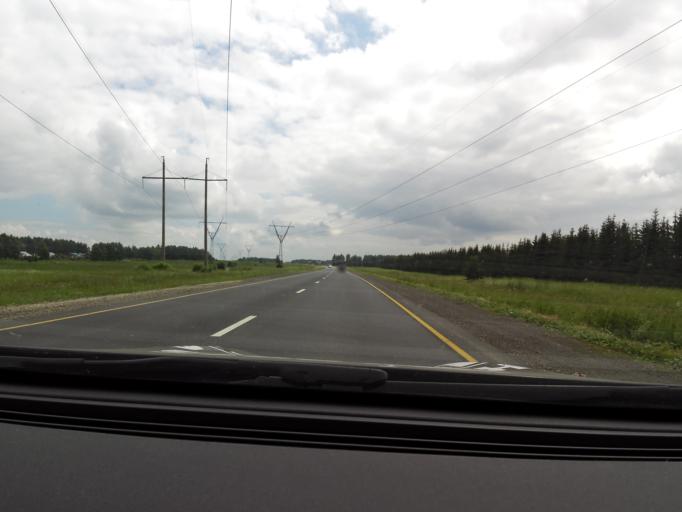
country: RU
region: Perm
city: Orda
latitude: 57.2618
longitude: 57.0247
